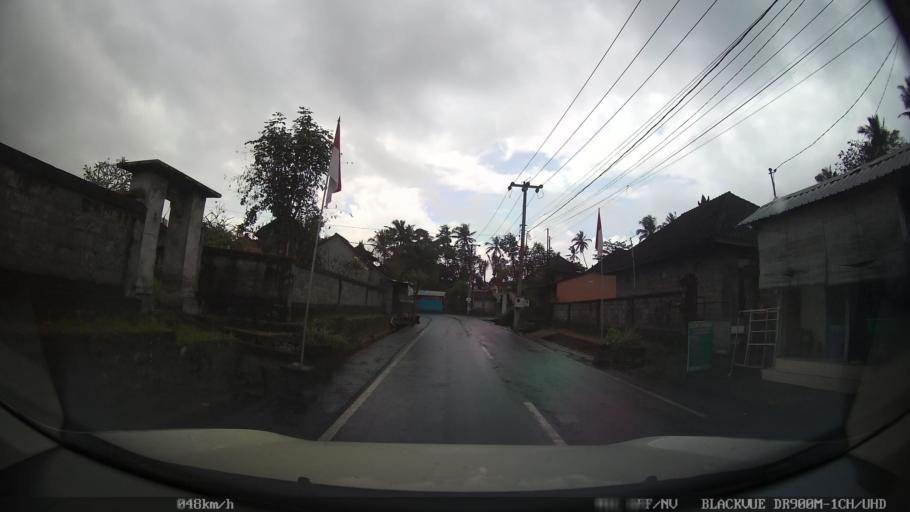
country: ID
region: Bali
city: Banjar Teguan
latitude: -8.5176
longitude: 115.2290
